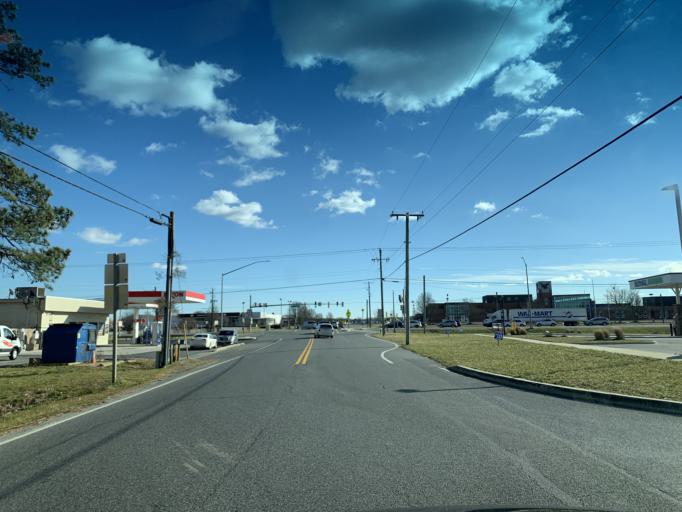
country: US
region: Maryland
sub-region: Worcester County
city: Berlin
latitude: 38.3442
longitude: -75.1908
